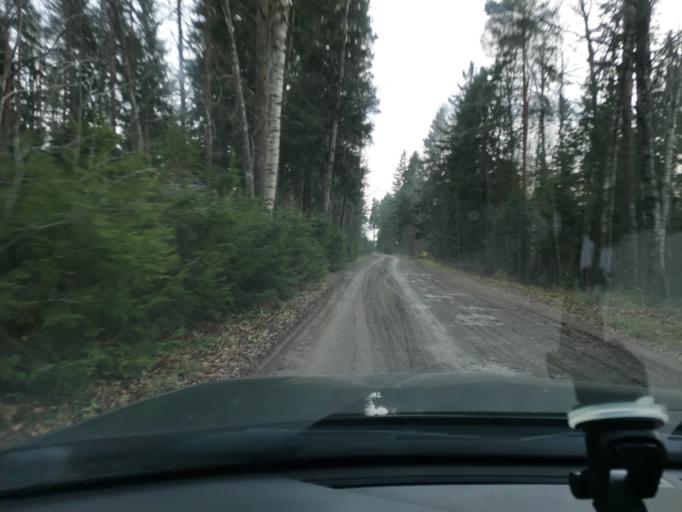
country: EE
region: Ida-Virumaa
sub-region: Sillamaee linn
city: Sillamae
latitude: 59.2558
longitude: 27.9134
